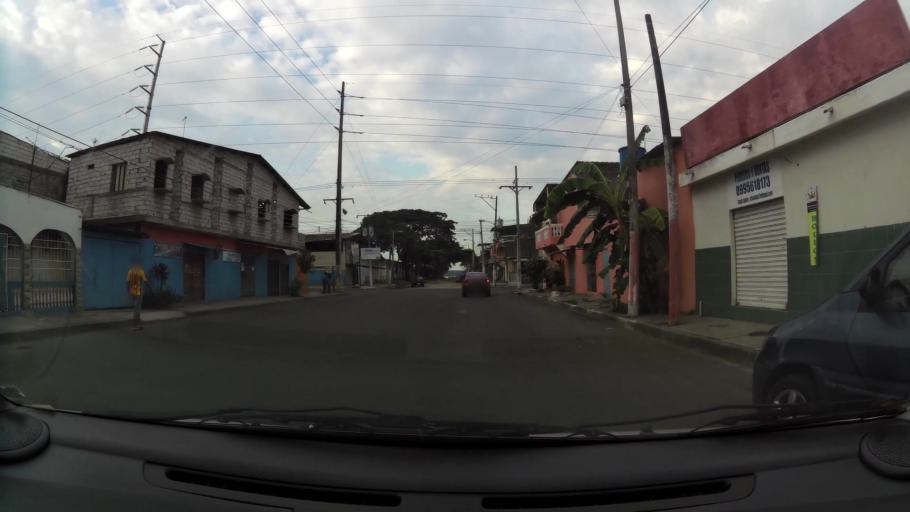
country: EC
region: Guayas
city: Guayaquil
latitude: -2.2501
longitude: -79.8793
